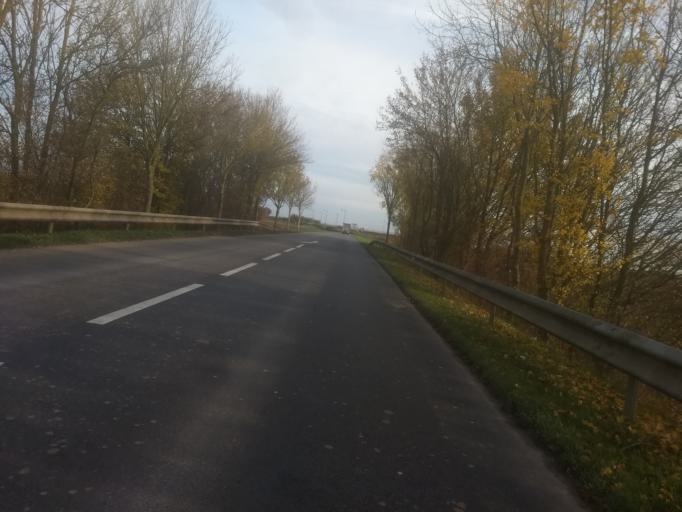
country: FR
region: Nord-Pas-de-Calais
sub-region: Departement du Pas-de-Calais
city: Agny
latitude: 50.2538
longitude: 2.7674
